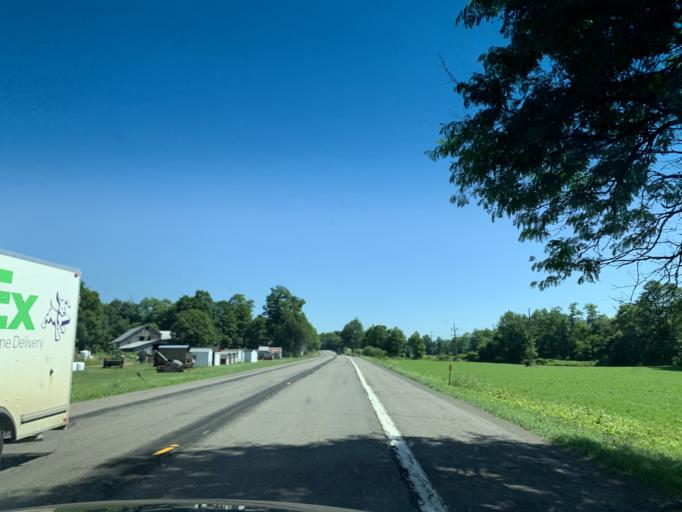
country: US
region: New York
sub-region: Delaware County
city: Sidney
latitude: 42.3916
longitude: -75.4017
